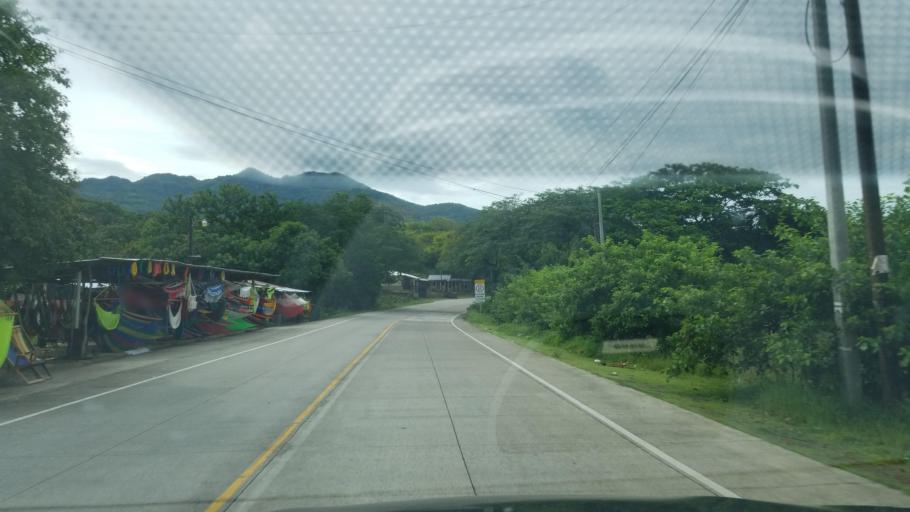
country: HN
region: Choluteca
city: Pespire
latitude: 13.6201
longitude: -87.3721
